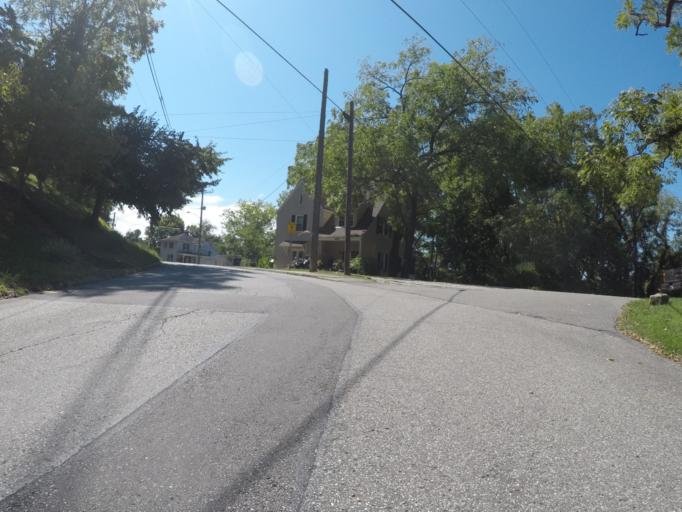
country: US
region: Kentucky
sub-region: Boyd County
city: Ashland
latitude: 38.4715
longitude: -82.6461
